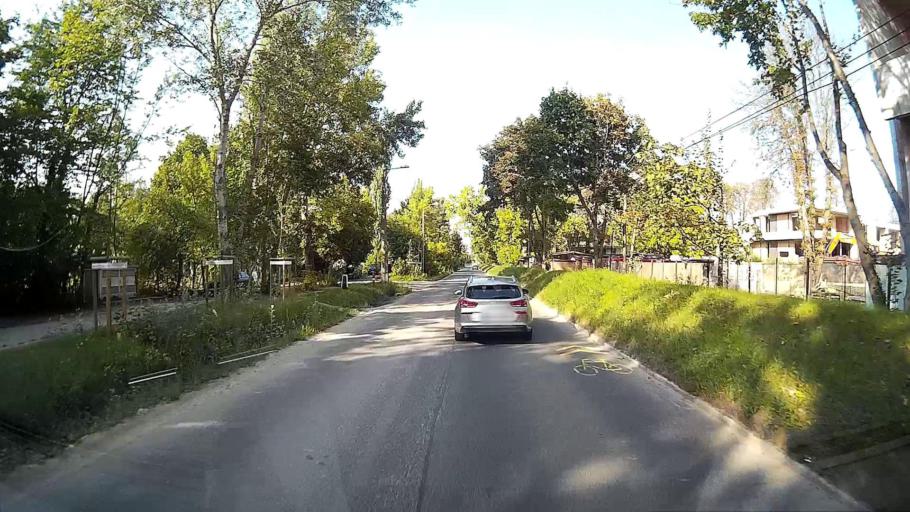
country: HU
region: Pest
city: Budakalasz
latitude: 47.5914
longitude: 19.0658
